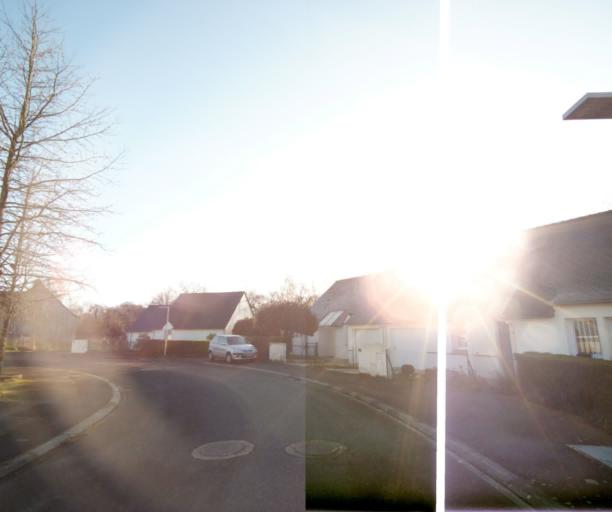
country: FR
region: Pays de la Loire
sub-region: Departement de la Loire-Atlantique
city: Bouvron
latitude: 47.4140
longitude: -1.8419
